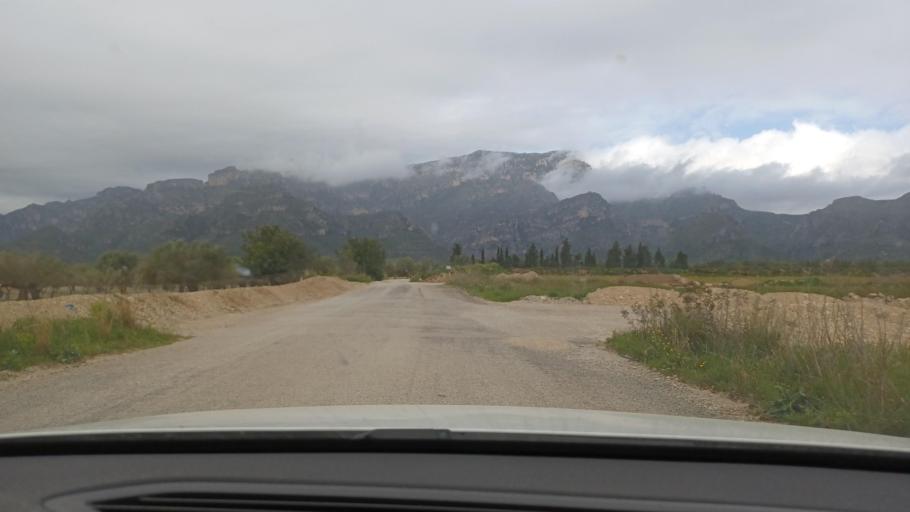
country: ES
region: Catalonia
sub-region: Provincia de Tarragona
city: Mas de Barberans
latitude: 40.7981
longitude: 0.4234
